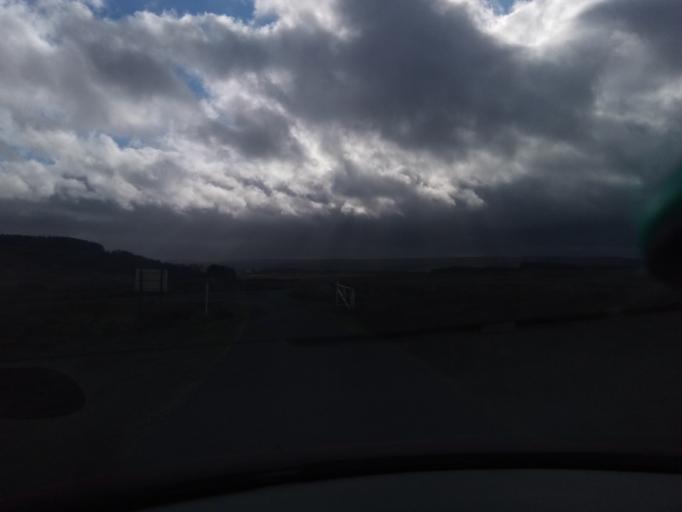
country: GB
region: England
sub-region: Northumberland
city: Rochester
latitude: 55.2985
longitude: -2.2807
